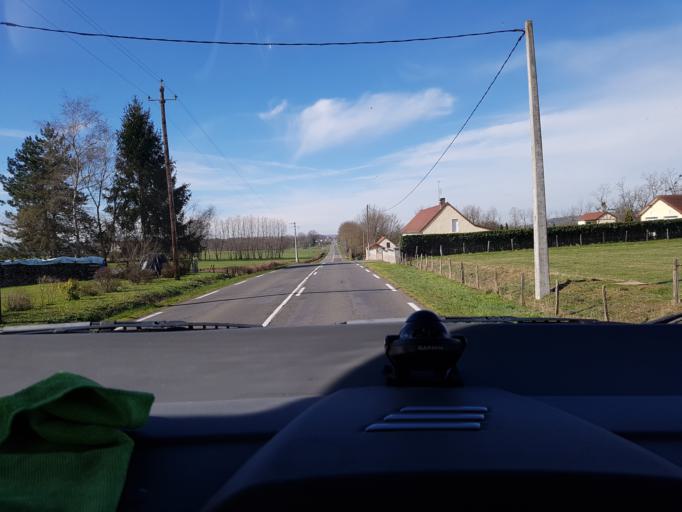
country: FR
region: Bourgogne
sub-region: Departement de Saone-et-Loire
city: Digoin
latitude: 46.5094
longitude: 4.0282
